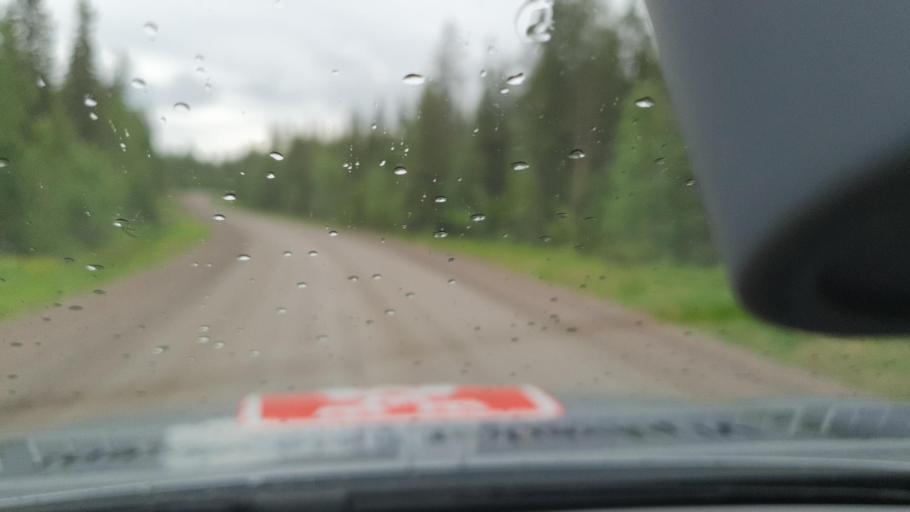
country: SE
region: Norrbotten
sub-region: Overtornea Kommun
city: OEvertornea
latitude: 66.4269
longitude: 23.5316
